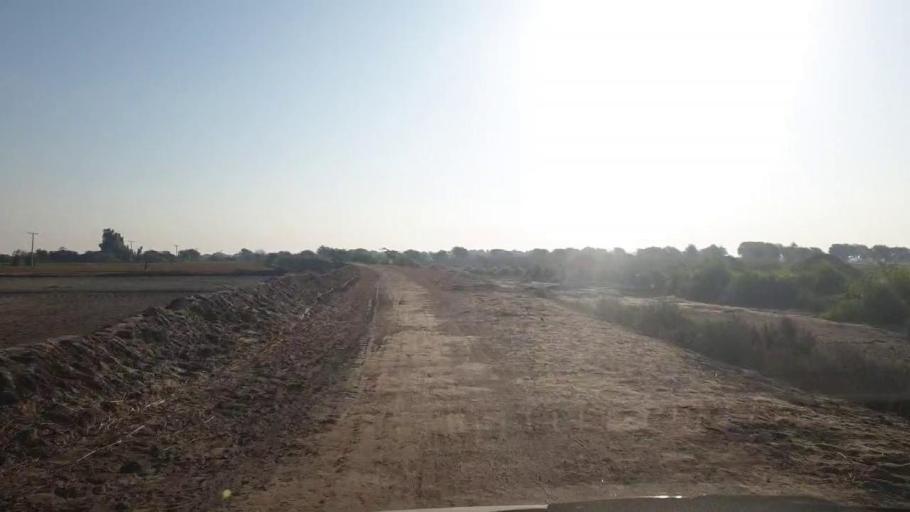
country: PK
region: Sindh
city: Talhar
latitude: 24.8083
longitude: 68.8403
